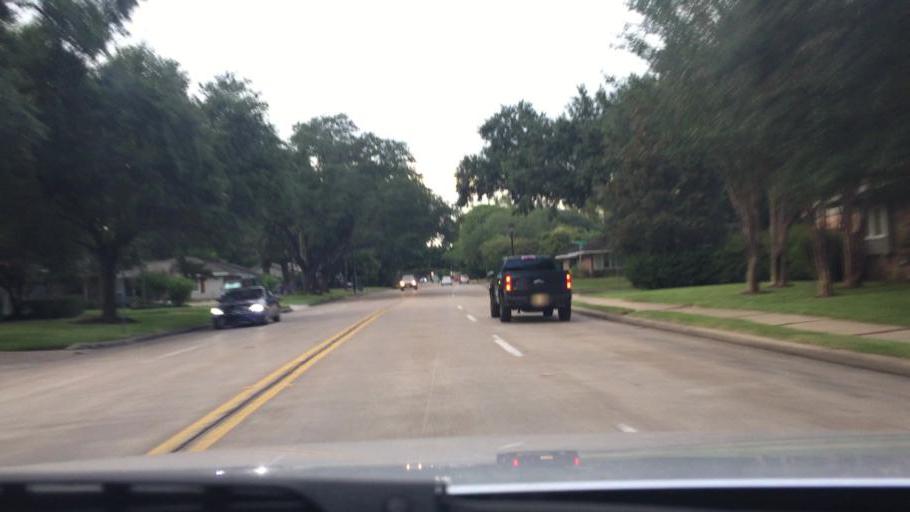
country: US
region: Texas
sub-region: Harris County
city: Hunters Creek Village
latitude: 29.7465
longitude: -95.4773
